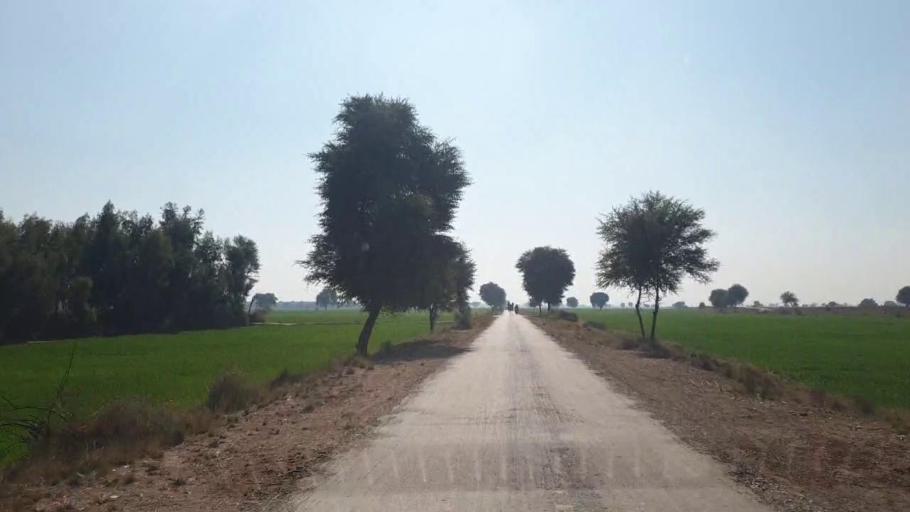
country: PK
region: Sindh
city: Shahpur Chakar
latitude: 26.1162
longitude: 68.6288
